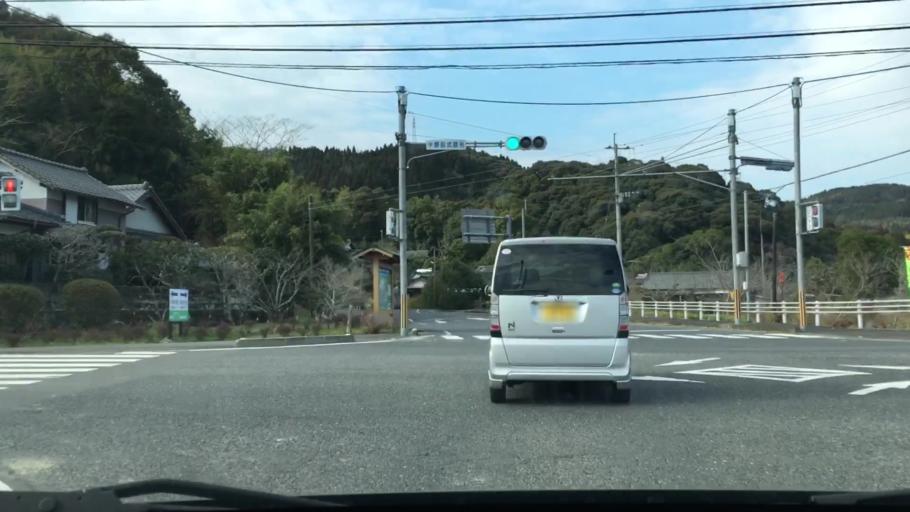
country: JP
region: Miyazaki
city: Nichinan
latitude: 31.6294
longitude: 131.3415
